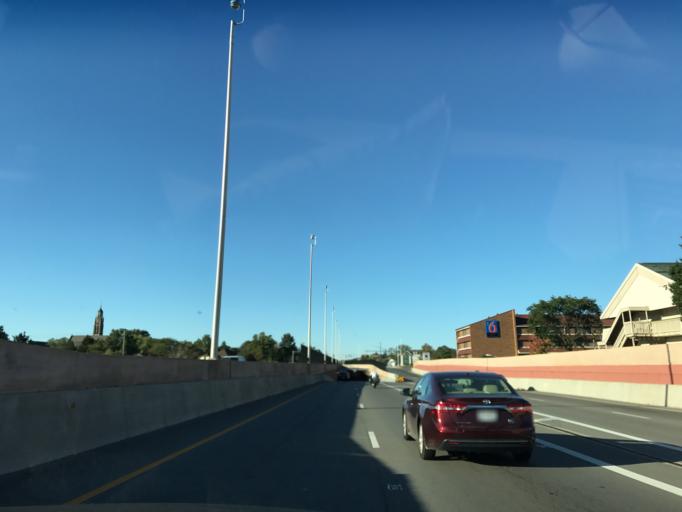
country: US
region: Ohio
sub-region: Franklin County
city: Worthington
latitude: 40.1149
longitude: -83.0163
